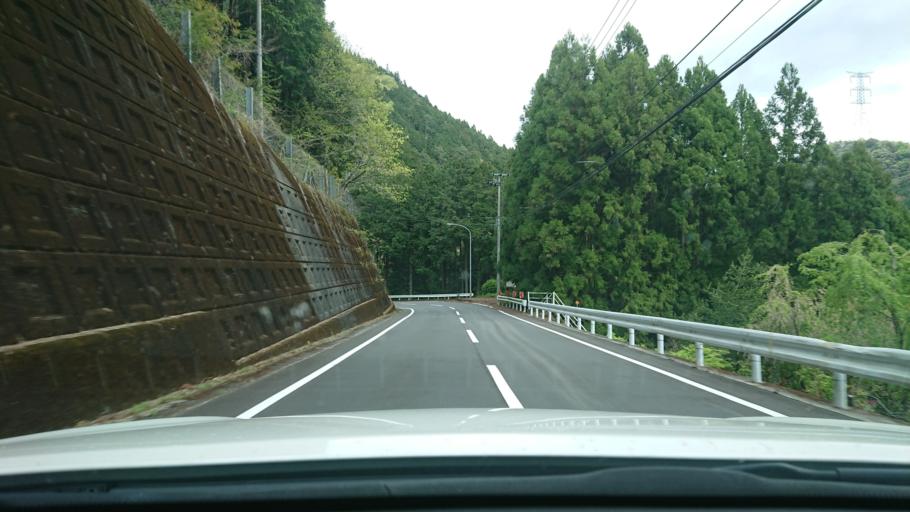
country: JP
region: Tokushima
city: Ishii
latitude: 33.9066
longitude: 134.4206
